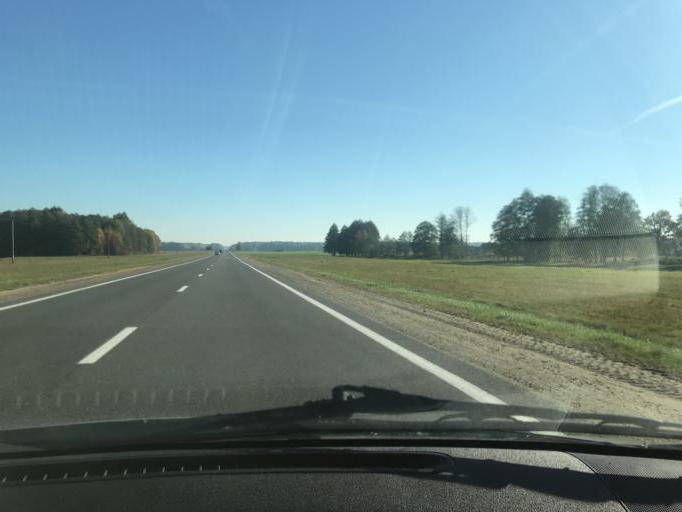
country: BY
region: Brest
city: Ivanava
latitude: 52.1560
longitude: 25.7014
